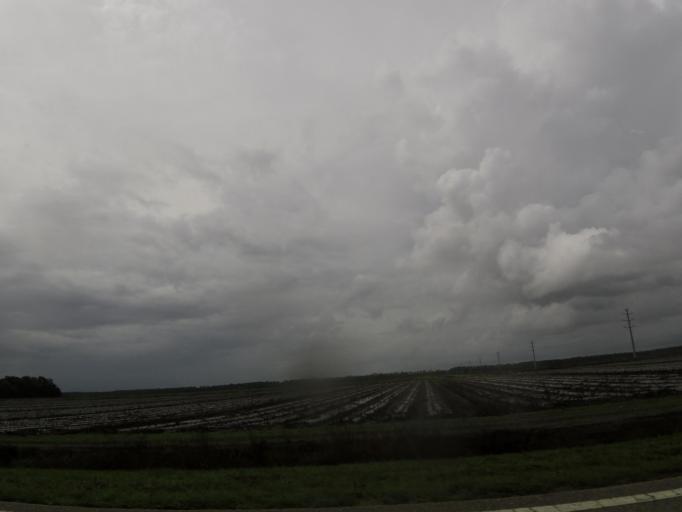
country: US
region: Florida
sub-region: Saint Johns County
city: Saint Augustine South
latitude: 29.8513
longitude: -81.5205
